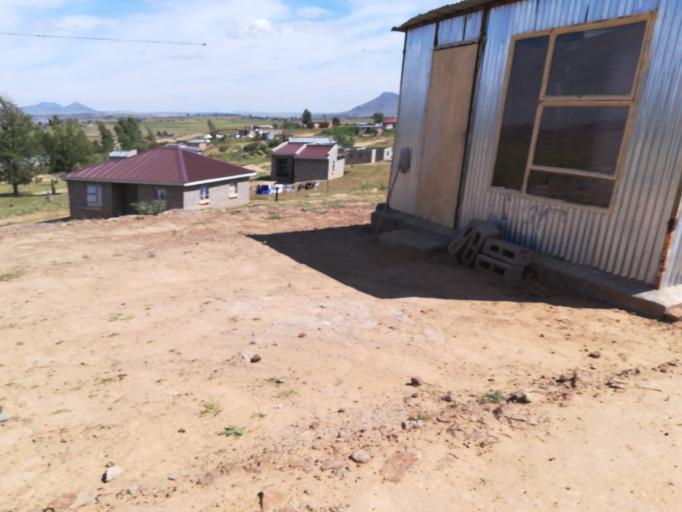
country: LS
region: Mohale's Hoek District
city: Mohale's Hoek
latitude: -30.1032
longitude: 27.4713
